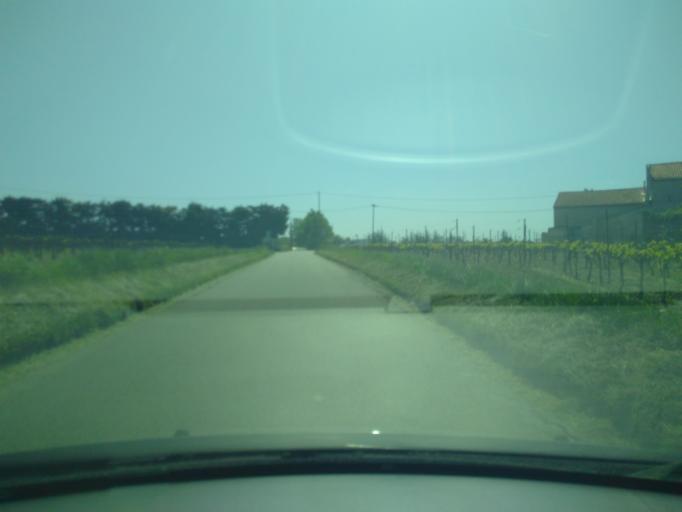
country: FR
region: Provence-Alpes-Cote d'Azur
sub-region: Departement du Vaucluse
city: Mazan
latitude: 44.0714
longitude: 5.0954
